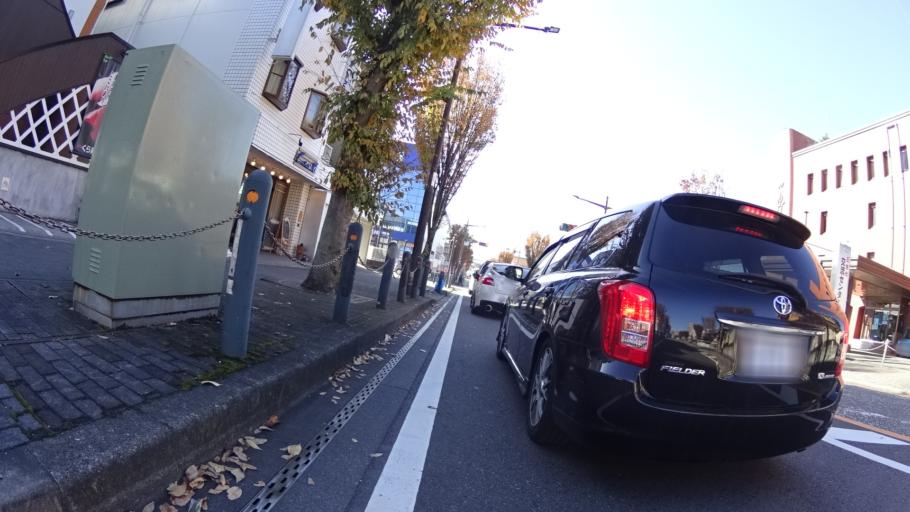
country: JP
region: Kanagawa
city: Zama
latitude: 35.5712
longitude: 139.3635
